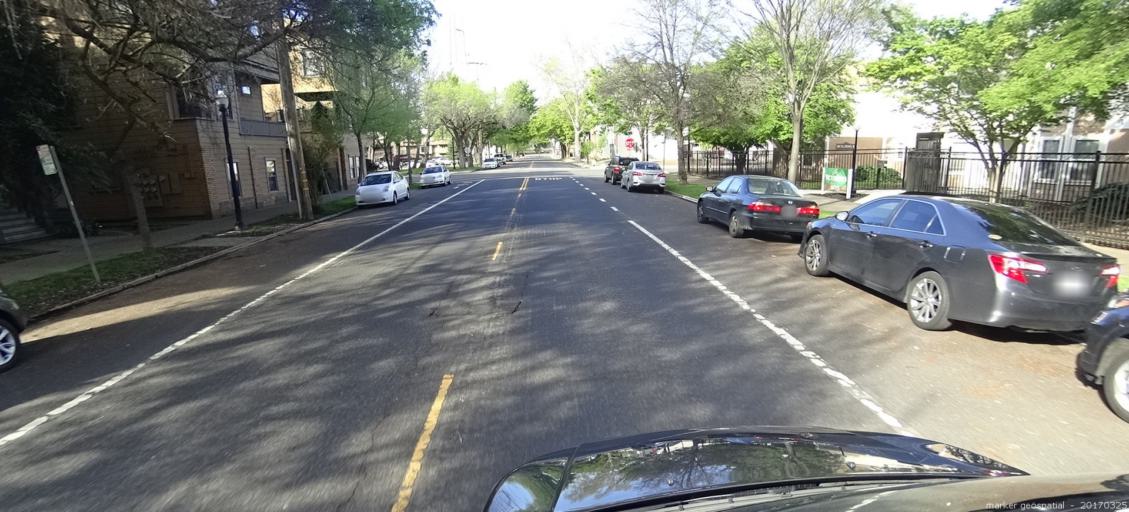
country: US
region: California
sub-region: Sacramento County
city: Sacramento
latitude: 38.5852
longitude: -121.4914
